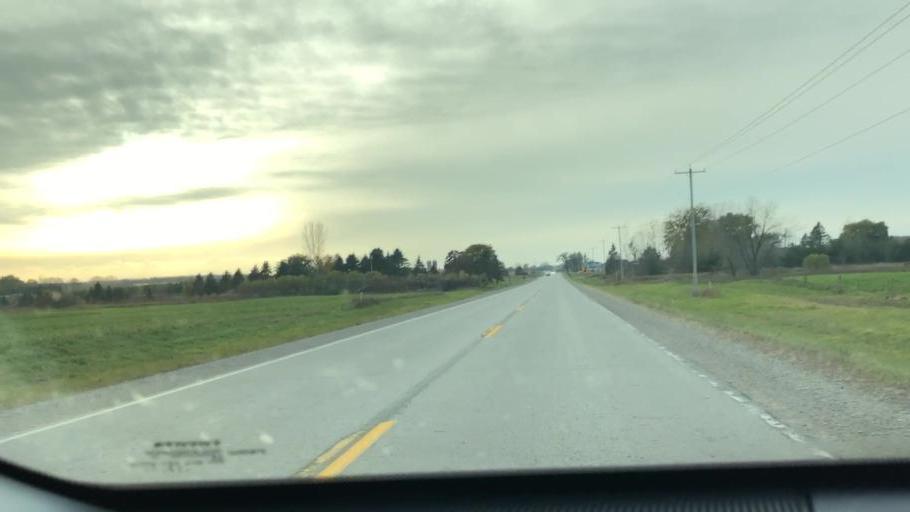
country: US
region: Wisconsin
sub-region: Outagamie County
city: Seymour
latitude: 44.4437
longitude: -88.3236
